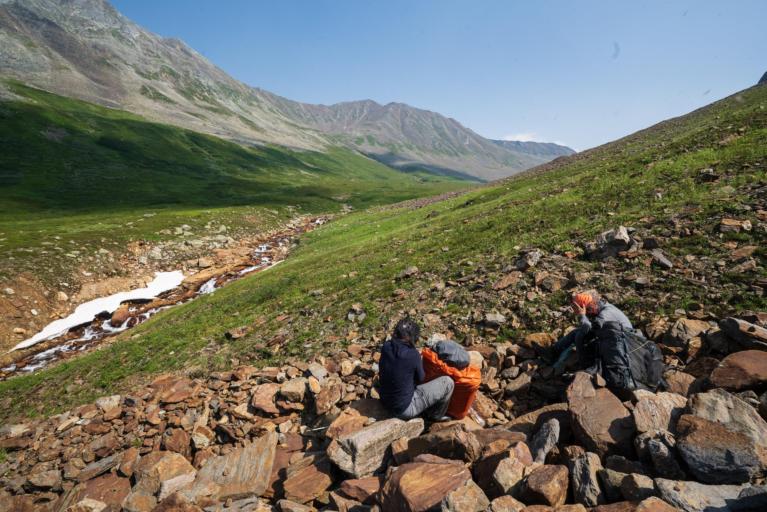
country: RU
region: Transbaikal Territory
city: Kuanda
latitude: 56.8100
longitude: 116.9152
